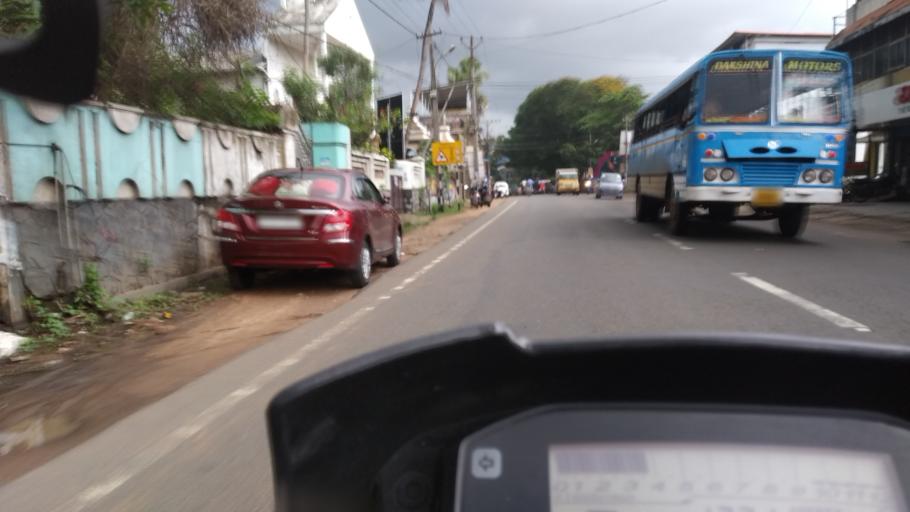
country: IN
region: Kerala
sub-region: Thiruvananthapuram
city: Attingal
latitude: 8.7025
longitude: 76.8142
